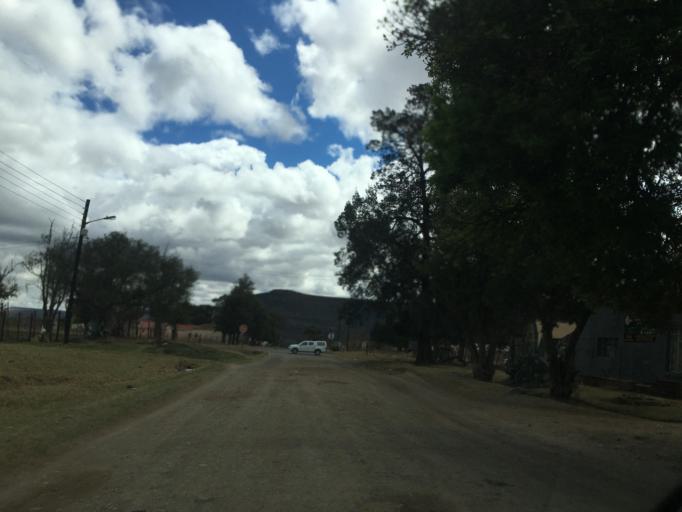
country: ZA
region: Eastern Cape
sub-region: Chris Hani District Municipality
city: Cala
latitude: -31.5215
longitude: 27.6990
